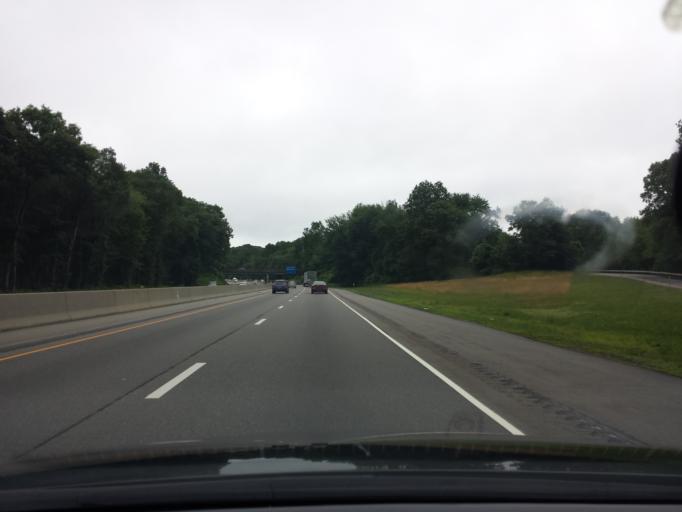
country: US
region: Connecticut
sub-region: New Haven County
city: Madison Center
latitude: 41.2877
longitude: -72.6059
